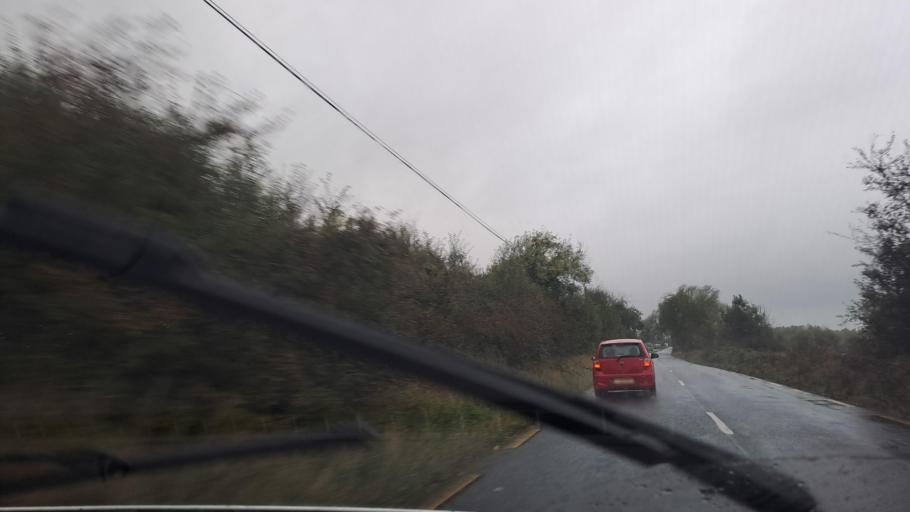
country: GB
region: Northern Ireland
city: Crossmaglen
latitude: 53.9709
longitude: -6.5889
